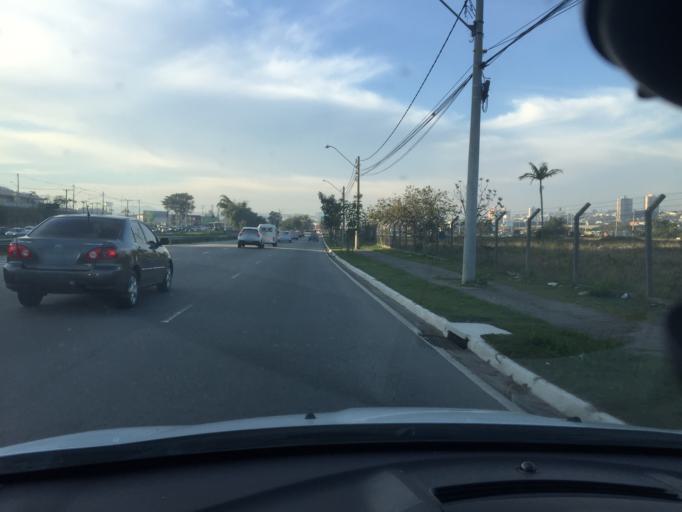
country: BR
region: Sao Paulo
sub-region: Jundiai
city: Jundiai
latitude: -23.1918
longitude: -46.8708
